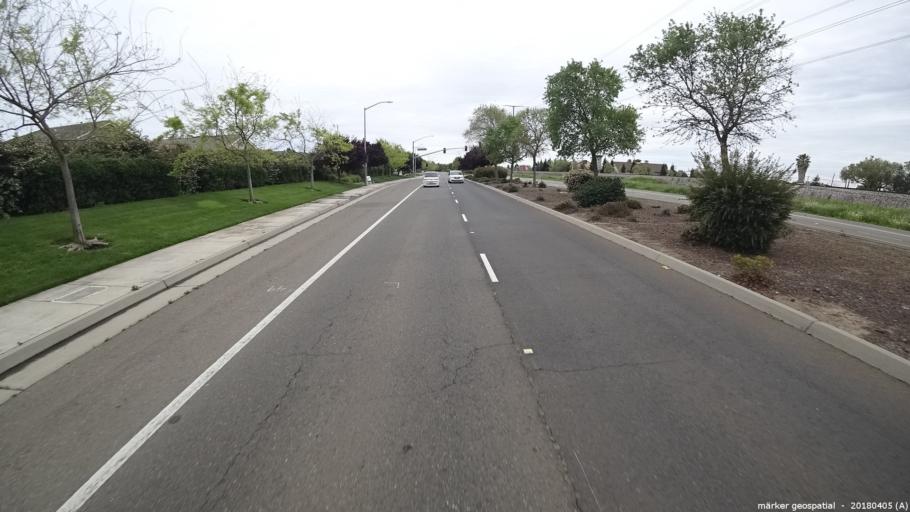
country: US
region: California
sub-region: Sacramento County
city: Laguna
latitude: 38.3883
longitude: -121.4516
